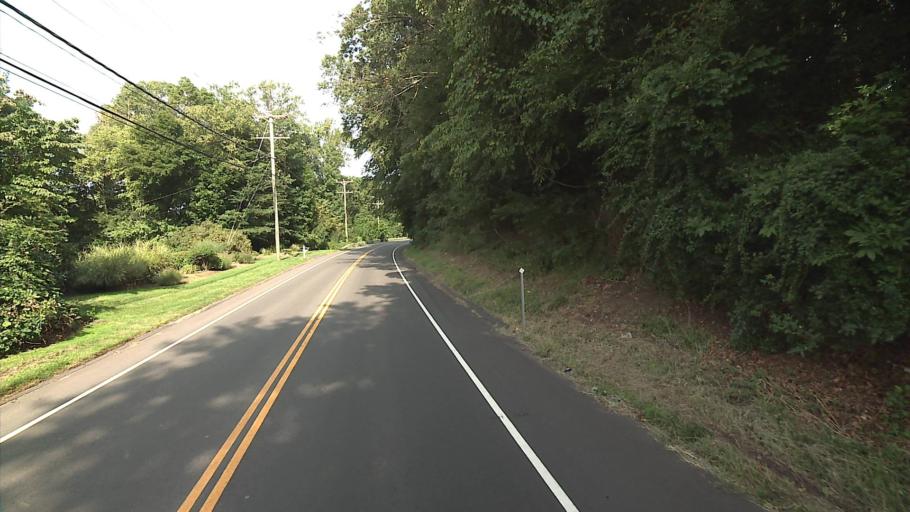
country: US
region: Connecticut
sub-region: Fairfield County
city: New Canaan
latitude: 41.1423
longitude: -73.4769
